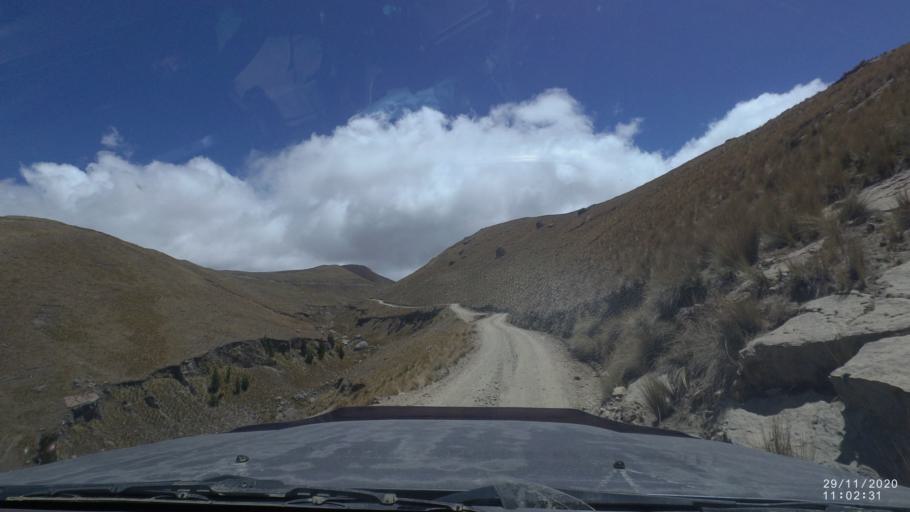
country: BO
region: Cochabamba
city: Cochabamba
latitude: -17.1948
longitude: -66.2249
